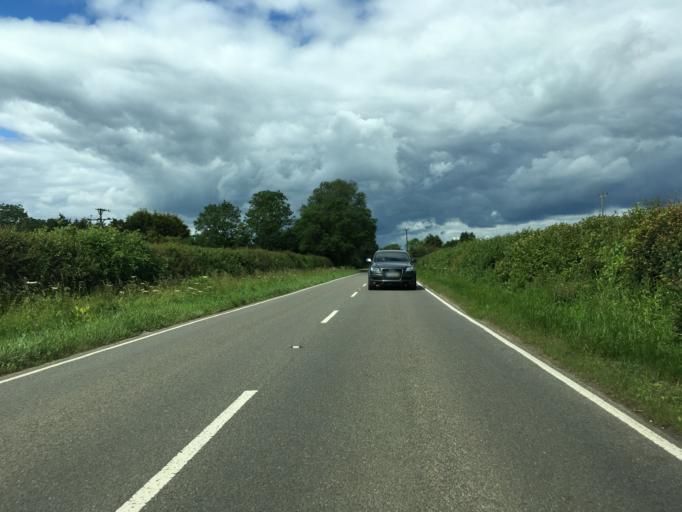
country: GB
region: England
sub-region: Northamptonshire
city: Brackley
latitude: 52.0791
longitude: -1.1552
